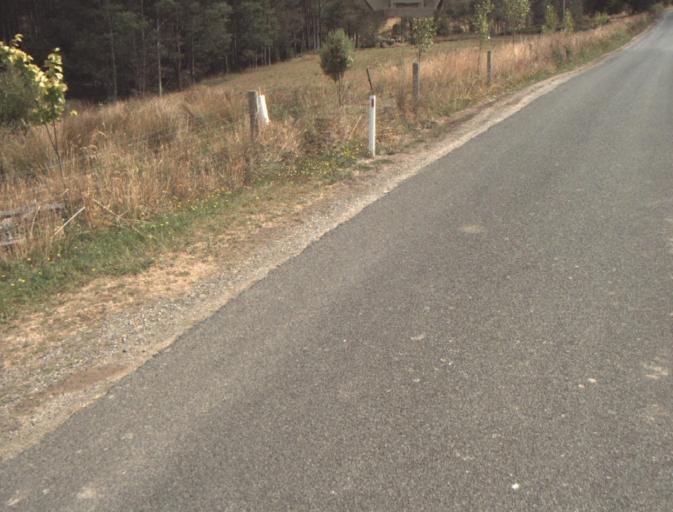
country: AU
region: Tasmania
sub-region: Launceston
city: Mayfield
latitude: -41.2591
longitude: 147.2076
